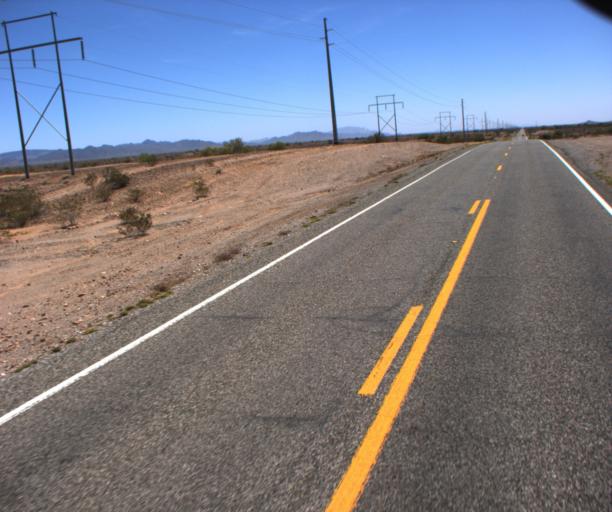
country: US
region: Arizona
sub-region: La Paz County
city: Quartzsite
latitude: 33.7669
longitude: -114.2170
